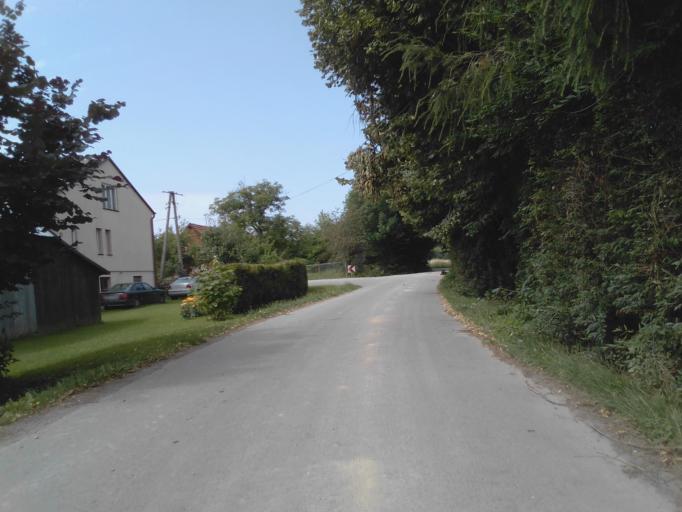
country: PL
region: Subcarpathian Voivodeship
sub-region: Powiat jasielski
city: Kolaczyce
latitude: 49.8256
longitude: 21.4935
